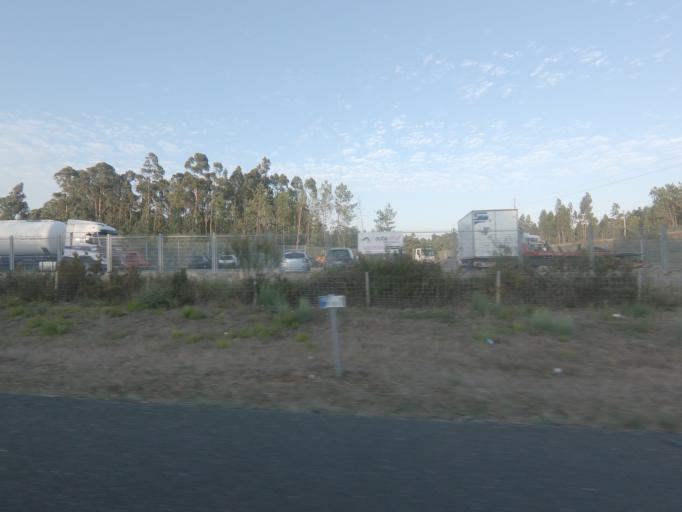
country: PT
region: Santarem
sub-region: Ourem
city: Fatima
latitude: 39.6293
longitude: -8.6977
